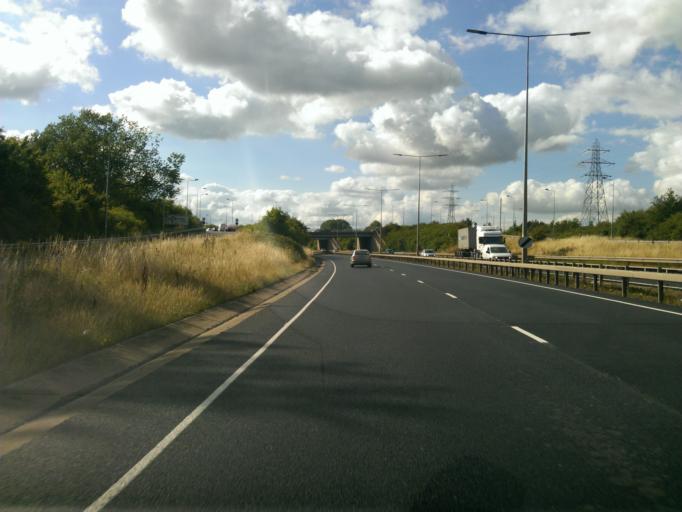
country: GB
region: England
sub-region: Staffordshire
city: Fazeley
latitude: 52.6185
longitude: -1.6685
